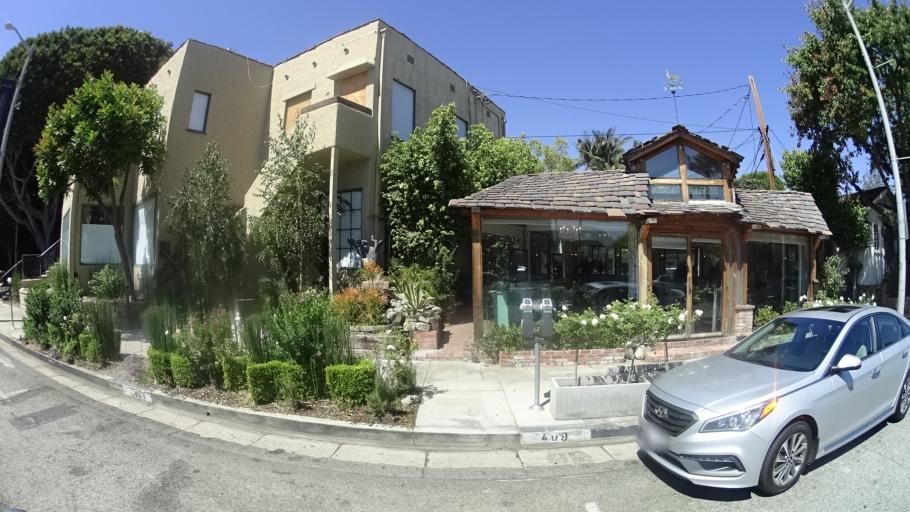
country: US
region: California
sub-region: Los Angeles County
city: Beverly Hills
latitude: 34.0790
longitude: -118.3845
